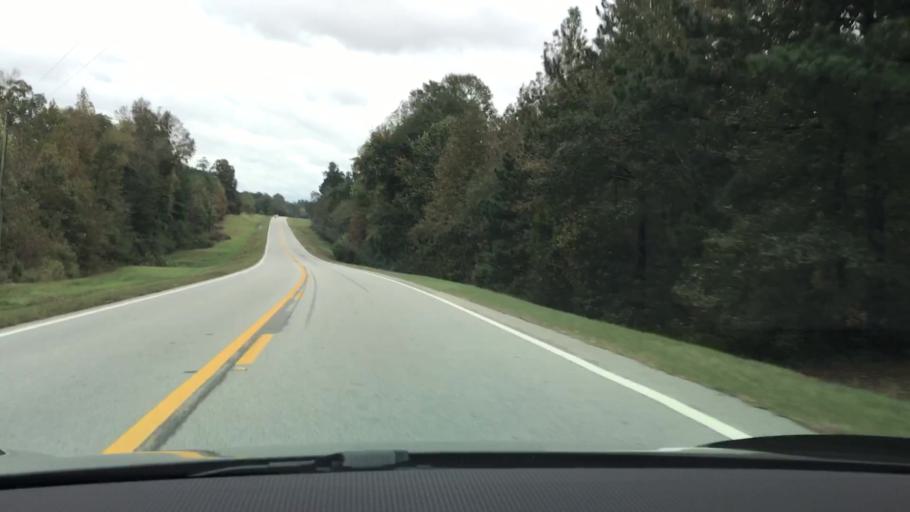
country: US
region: Georgia
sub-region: Glascock County
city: Gibson
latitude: 33.2649
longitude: -82.4894
